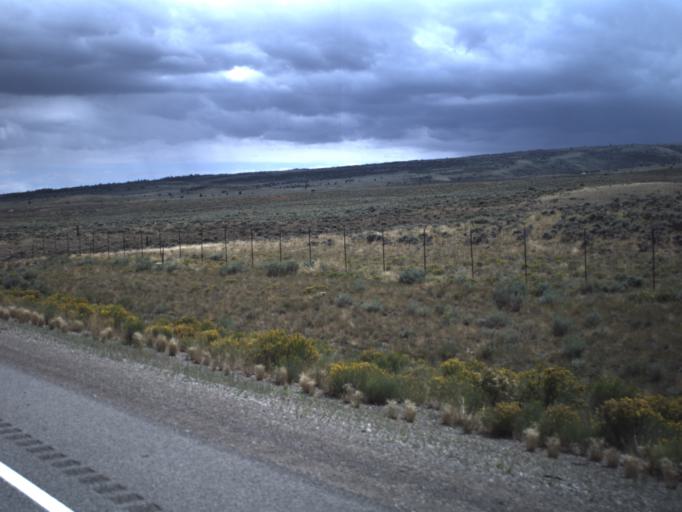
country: US
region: Utah
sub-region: Carbon County
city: Helper
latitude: 39.8408
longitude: -110.9885
